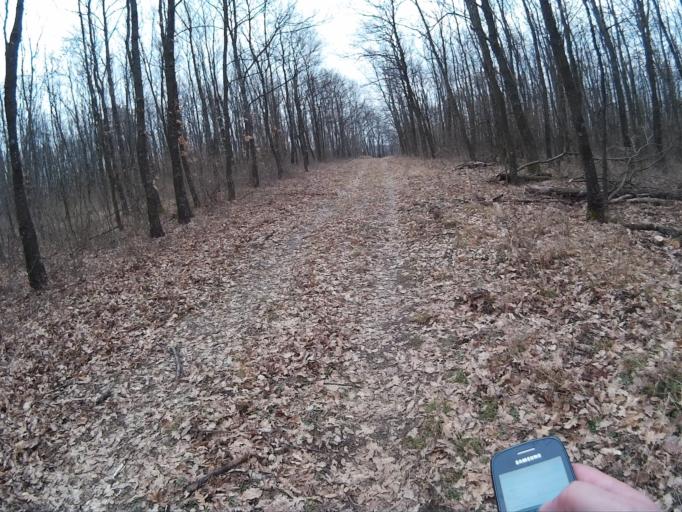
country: HU
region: Veszprem
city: Zirc
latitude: 47.1871
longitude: 17.9186
